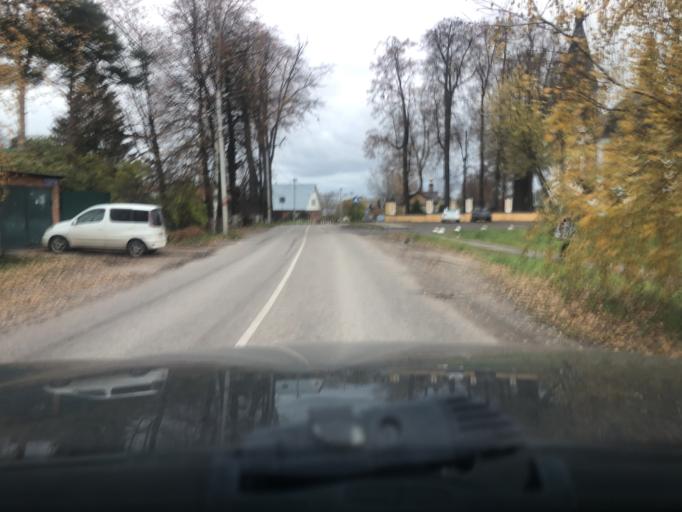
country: RU
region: Moskovskaya
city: Sergiyev Posad
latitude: 56.2988
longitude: 38.1238
